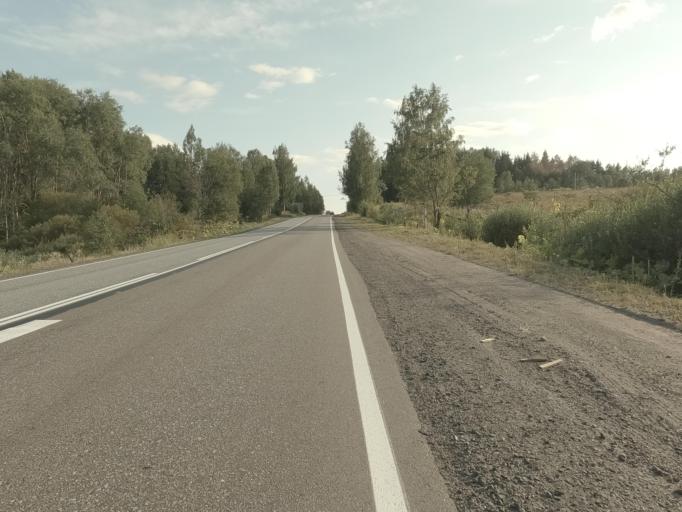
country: RU
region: Leningrad
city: Vyborg
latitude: 60.8375
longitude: 28.8385
